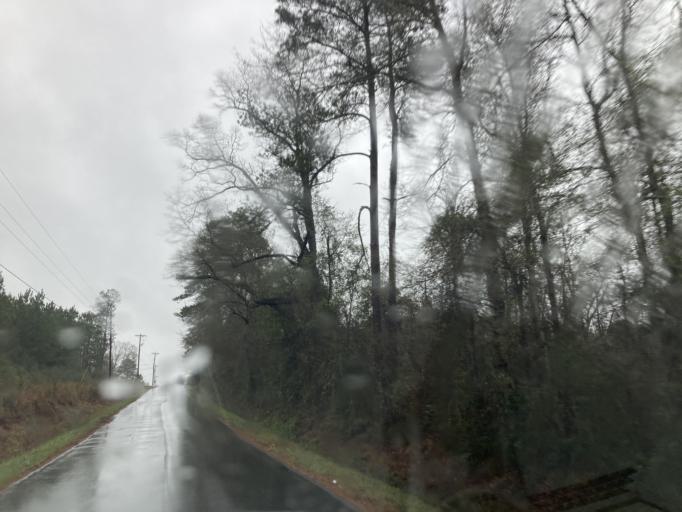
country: US
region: Mississippi
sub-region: Forrest County
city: Rawls Springs
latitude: 31.4799
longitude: -89.3823
